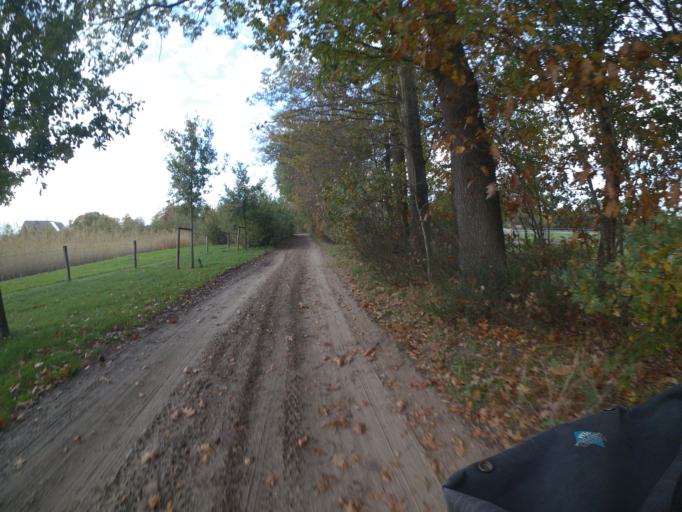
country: NL
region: North Brabant
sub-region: Gemeente Vught
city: Vught
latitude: 51.6182
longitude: 5.2695
